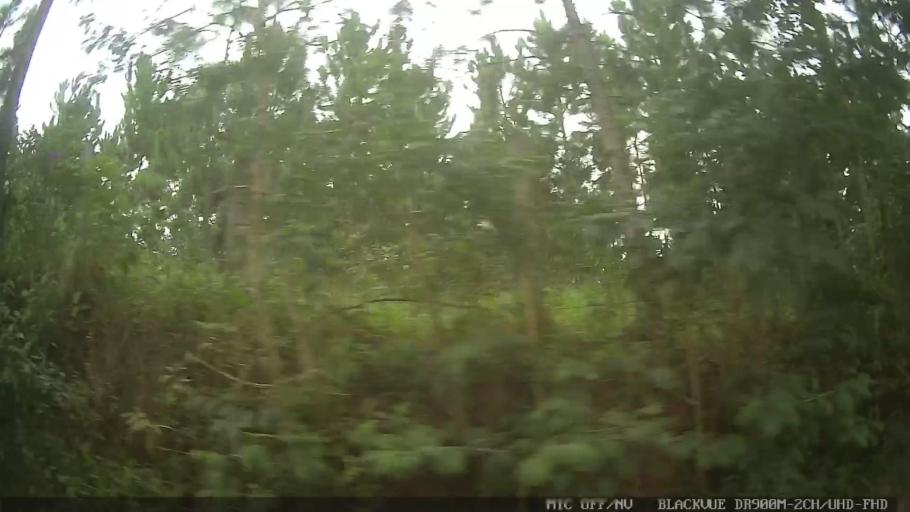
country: BR
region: Sao Paulo
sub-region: Atibaia
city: Atibaia
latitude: -23.1844
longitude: -46.6019
